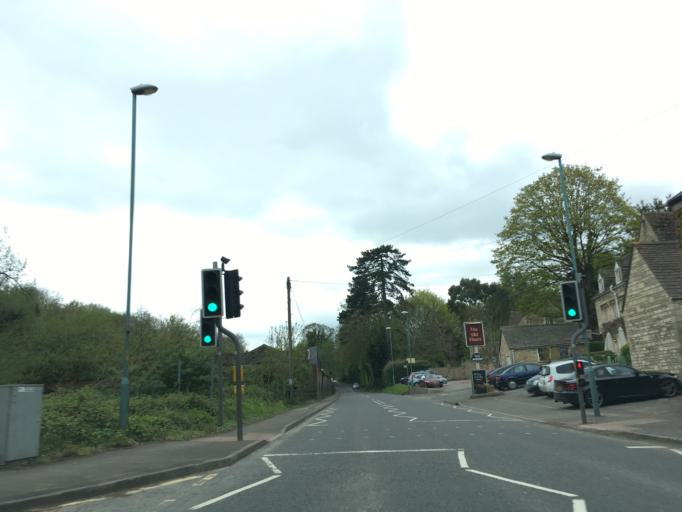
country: GB
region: England
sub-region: Gloucestershire
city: Nailsworth
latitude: 51.7259
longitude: -2.2297
